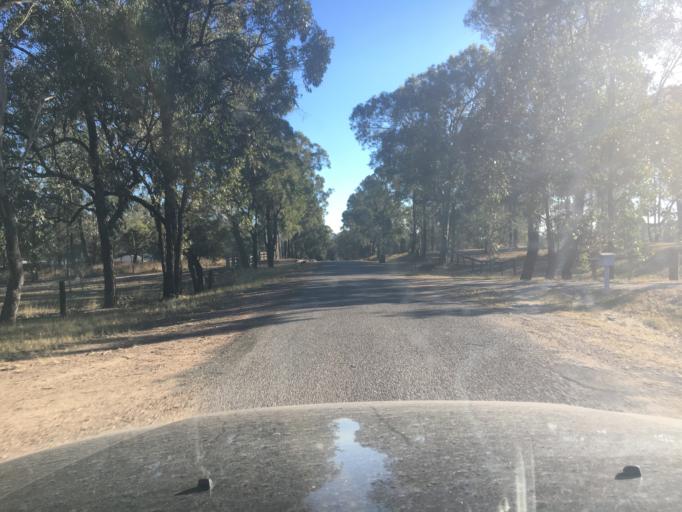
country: AU
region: New South Wales
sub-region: Singleton
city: Singleton
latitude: -32.5510
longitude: 151.2371
